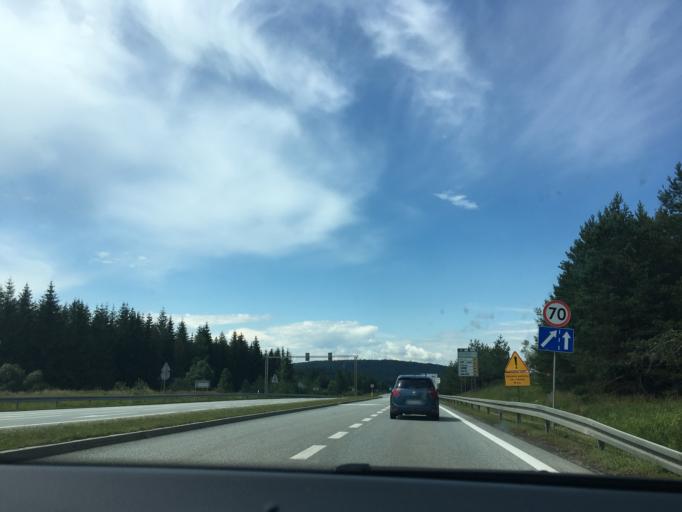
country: PL
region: Subcarpathian Voivodeship
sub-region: Powiat krosnienski
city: Jasliska
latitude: 49.4203
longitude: 21.6947
